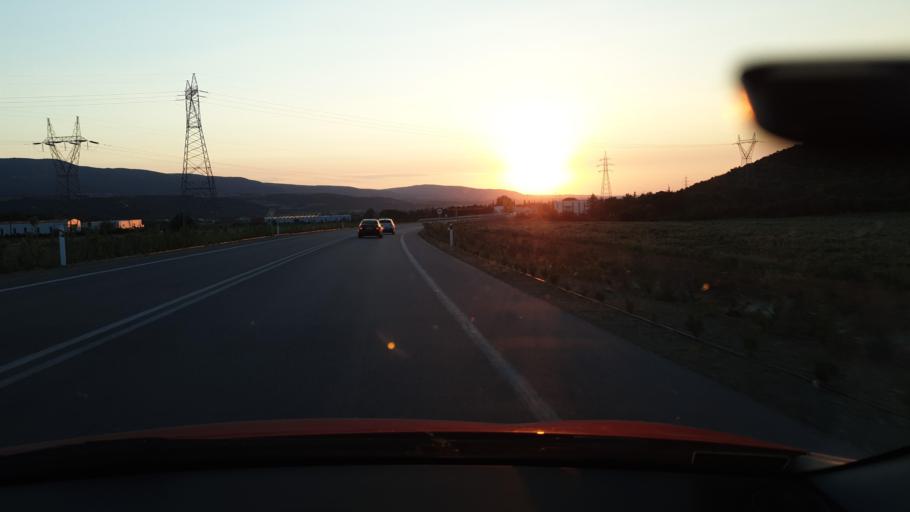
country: GR
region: Central Macedonia
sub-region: Nomos Thessalonikis
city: Vasilika
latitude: 40.4661
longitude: 23.2041
